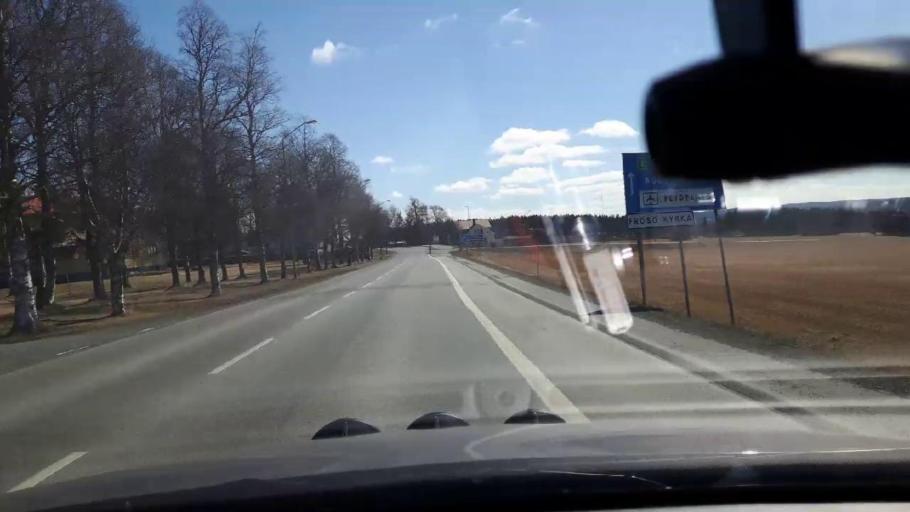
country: SE
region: Jaemtland
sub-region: OEstersunds Kommun
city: Ostersund
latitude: 63.1802
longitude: 14.5172
